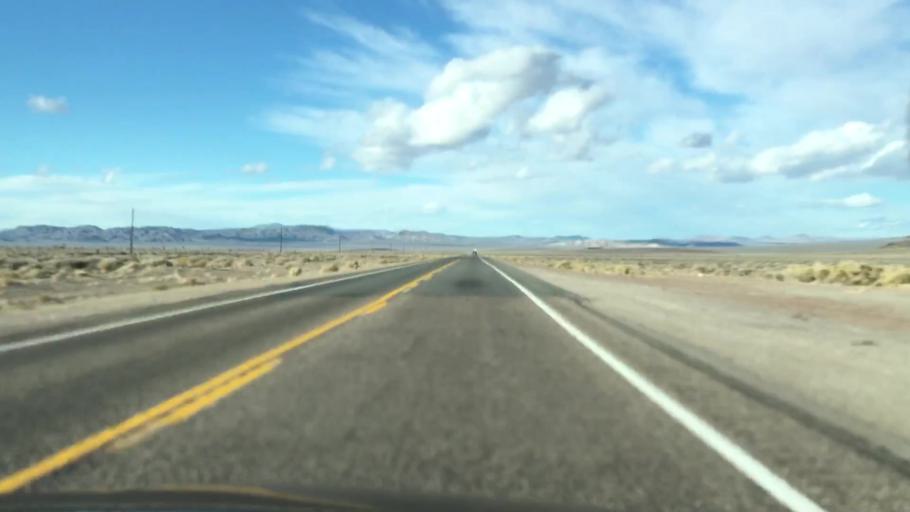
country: US
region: Nevada
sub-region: Esmeralda County
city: Goldfield
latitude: 37.3935
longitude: -117.1460
